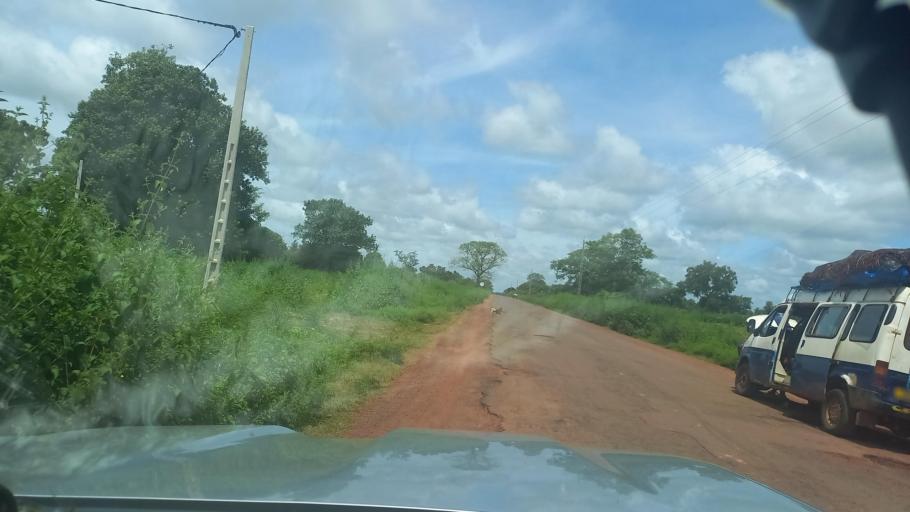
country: GM
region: Lower River
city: Kaiaf
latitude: 13.2228
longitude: -15.5403
